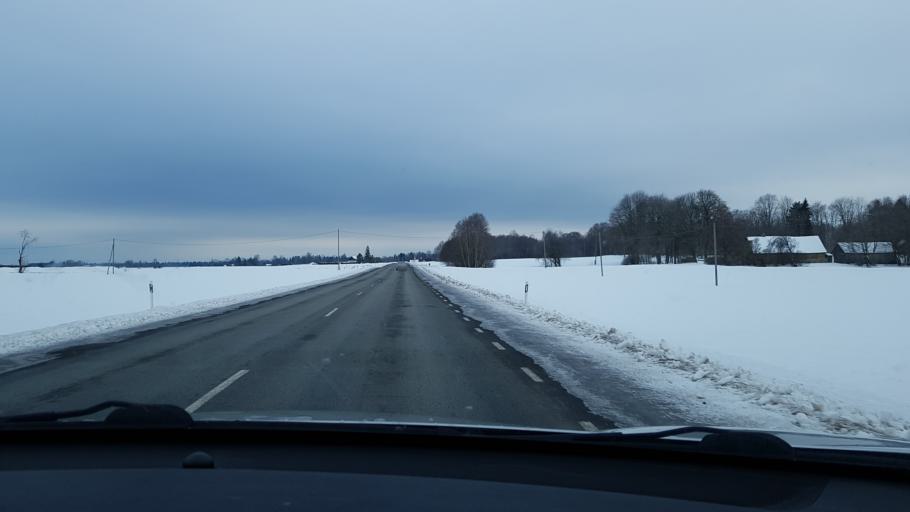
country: EE
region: Jaervamaa
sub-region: Paide linn
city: Paide
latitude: 58.8853
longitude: 25.7088
